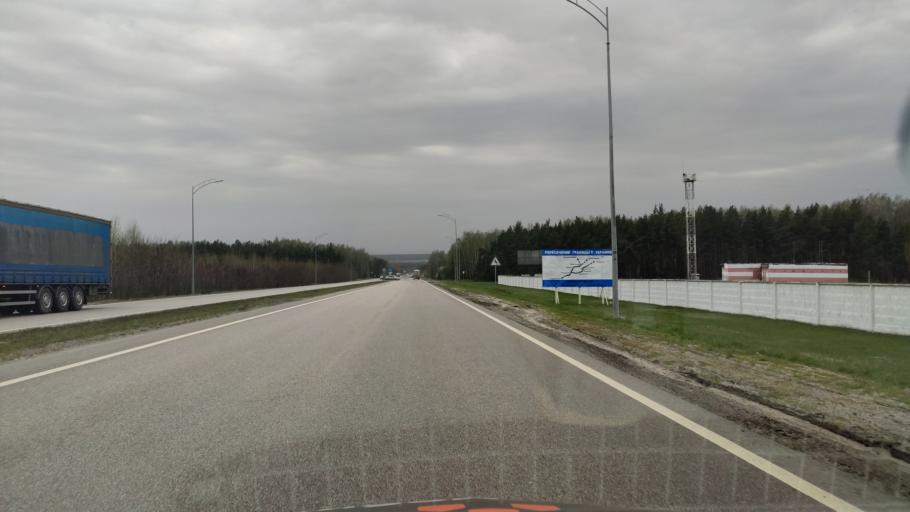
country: RU
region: Belgorod
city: Staryy Oskol
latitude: 51.3690
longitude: 37.8439
